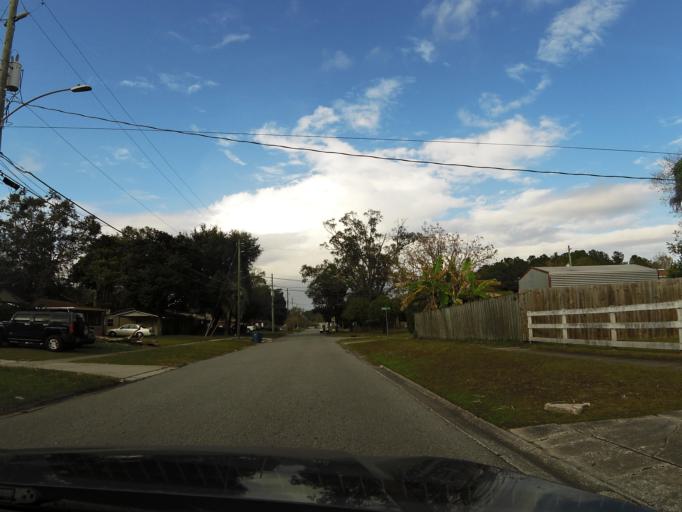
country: US
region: Florida
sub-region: Duval County
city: Jacksonville
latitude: 30.3457
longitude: -81.5650
